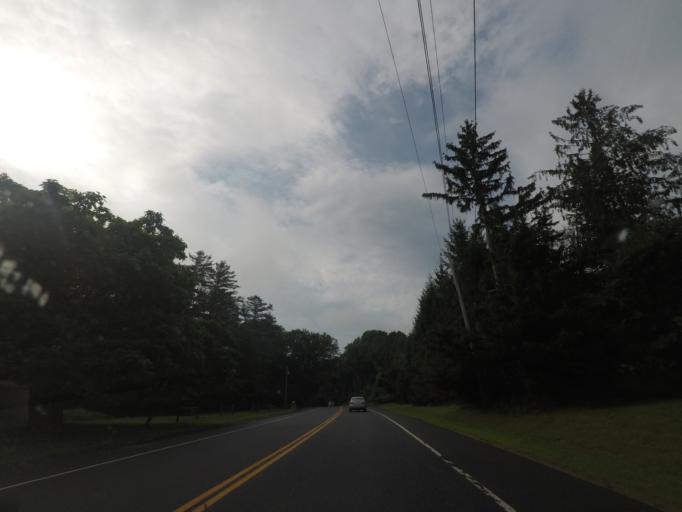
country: US
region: New York
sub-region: Rensselaer County
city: Nassau
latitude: 42.5042
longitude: -73.5608
